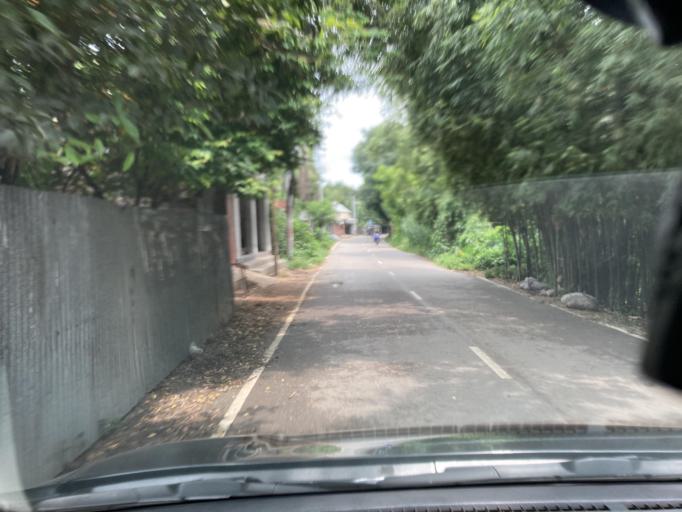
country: BD
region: Dhaka
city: Dohar
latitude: 23.7676
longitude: 90.1970
